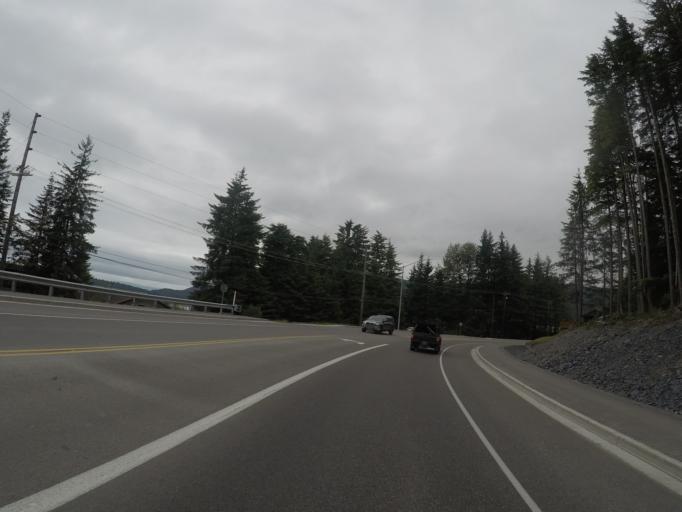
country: US
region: Alaska
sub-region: Juneau City and Borough
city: Juneau
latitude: 58.3817
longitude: -134.6434
